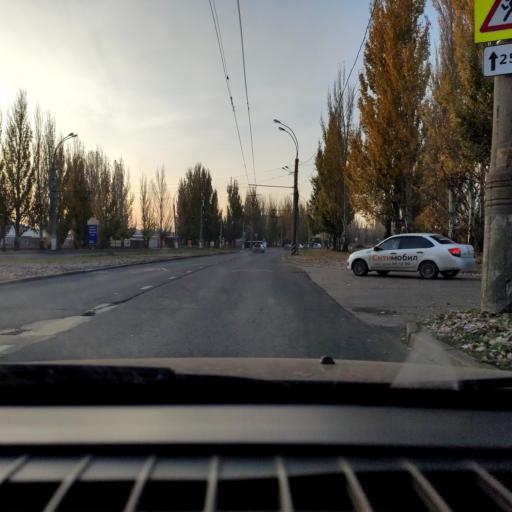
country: RU
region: Samara
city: Tol'yatti
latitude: 53.5430
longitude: 49.2788
